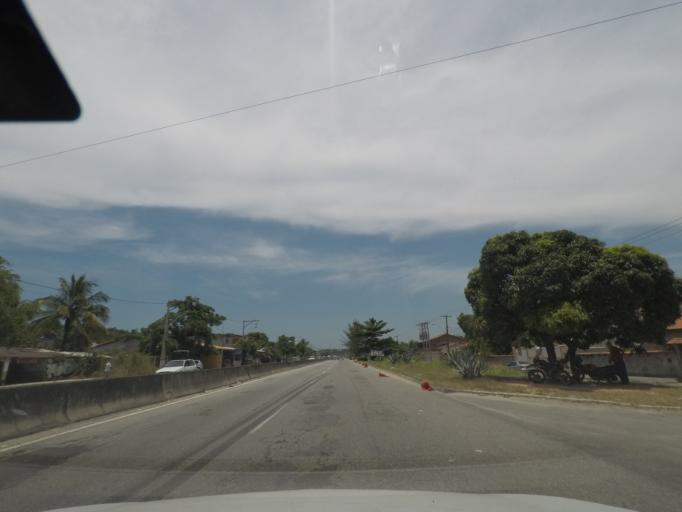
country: BR
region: Rio de Janeiro
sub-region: Marica
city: Marica
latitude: -22.9248
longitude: -42.8635
